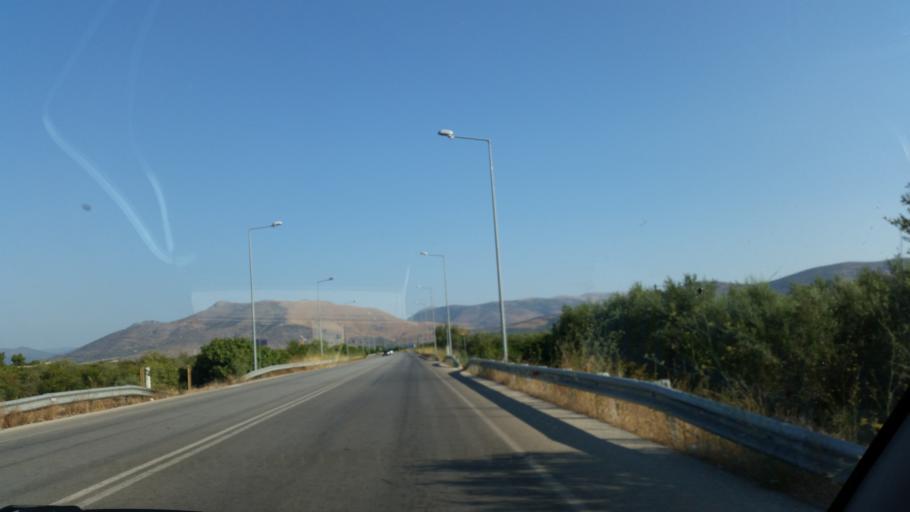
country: GR
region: Peloponnese
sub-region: Nomos Argolidos
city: Ayia Trias
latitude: 37.6358
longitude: 22.8171
